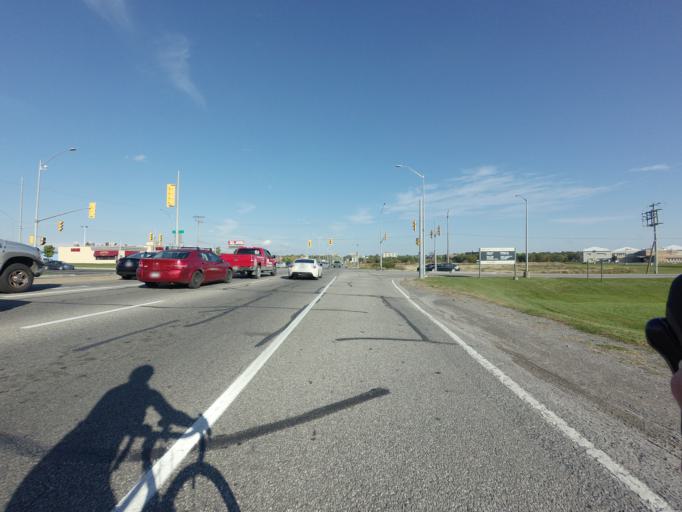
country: CA
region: Ontario
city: Kingston
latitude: 44.2374
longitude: -76.5490
